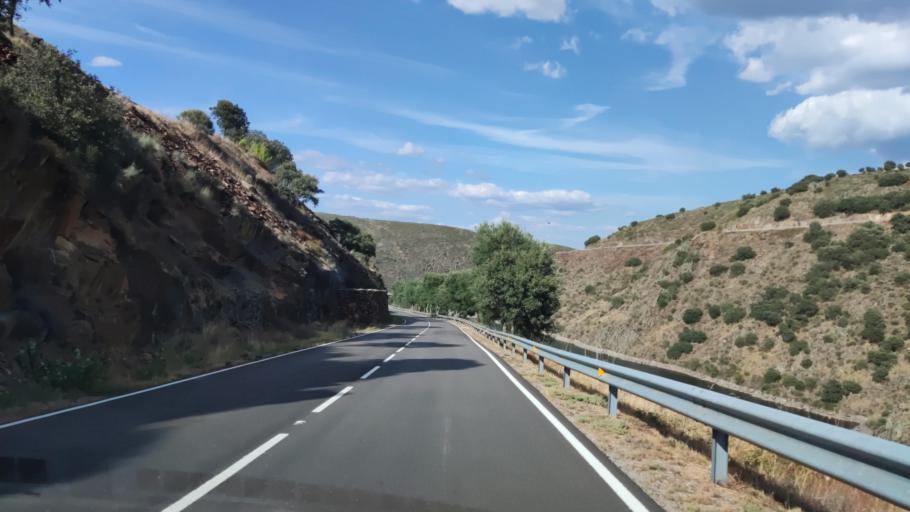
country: ES
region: Castille and Leon
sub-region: Provincia de Salamanca
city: Pastores
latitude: 40.4933
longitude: -6.4990
